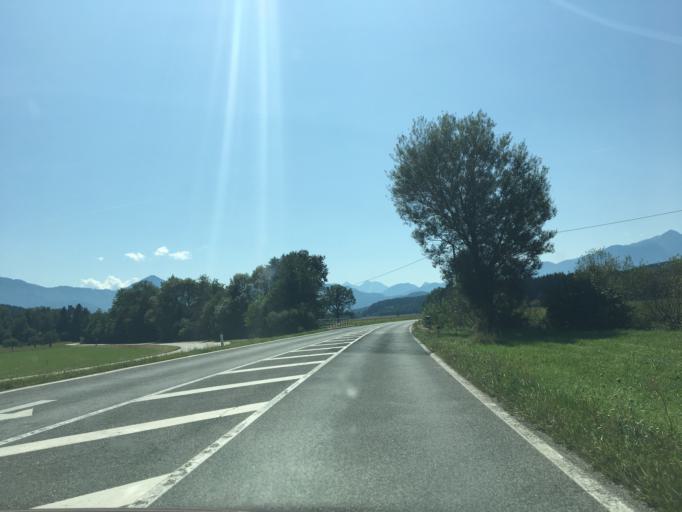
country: AT
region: Carinthia
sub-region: Politischer Bezirk Volkermarkt
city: Eberndorf
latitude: 46.6098
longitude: 14.6354
